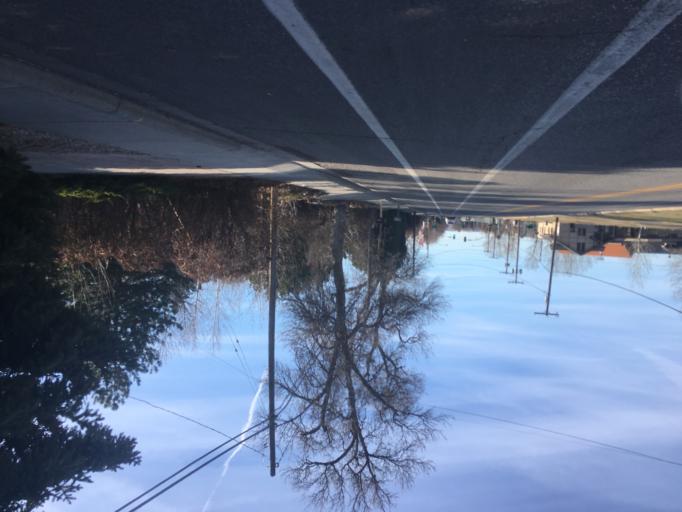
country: US
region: Montana
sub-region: Yellowstone County
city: Billings
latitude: 45.7950
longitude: -108.5615
